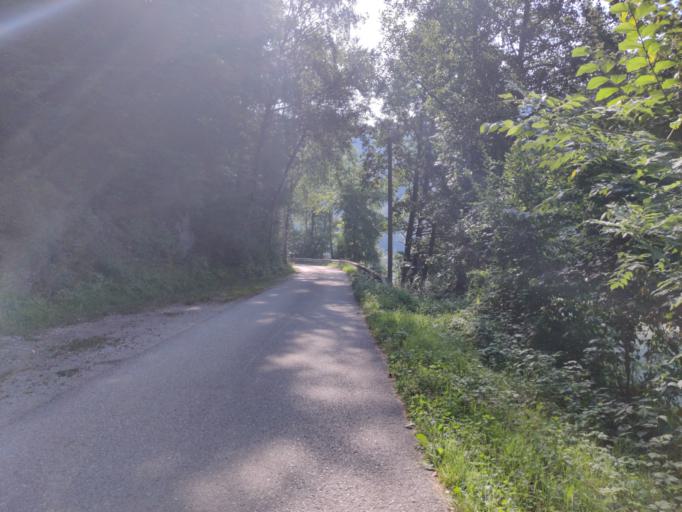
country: AT
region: Upper Austria
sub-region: Politischer Bezirk Rohrbach
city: Kleinzell im Muehlkreis
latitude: 48.4181
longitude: 13.9665
